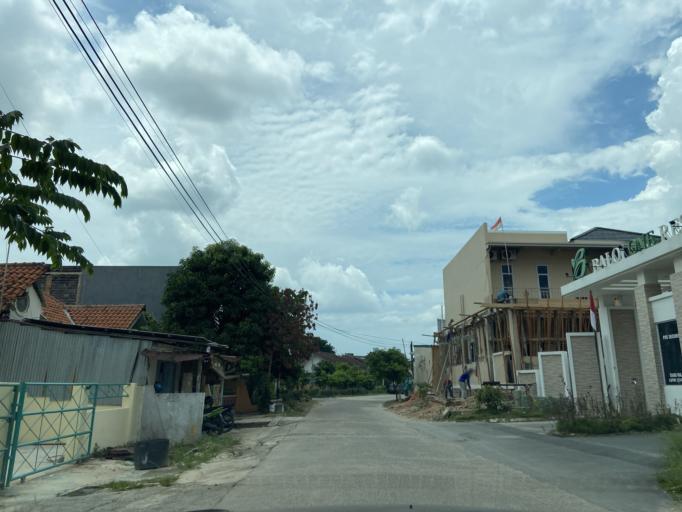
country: SG
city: Singapore
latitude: 1.1265
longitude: 104.0136
